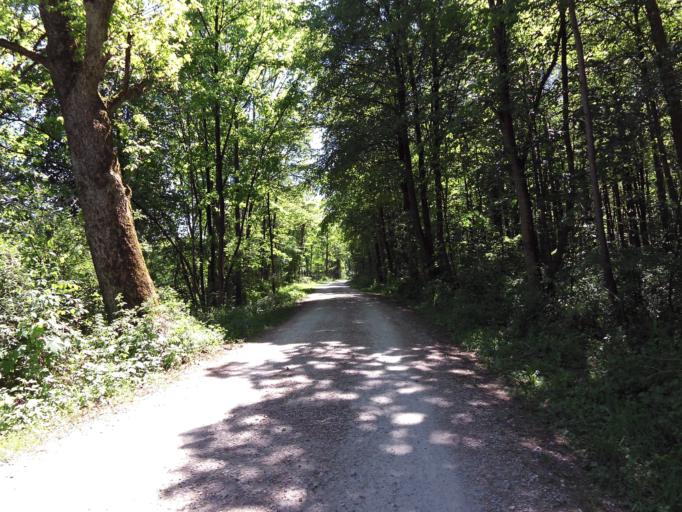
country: DE
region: Bavaria
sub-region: Upper Bavaria
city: Ismaning
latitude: 48.2366
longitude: 11.6718
